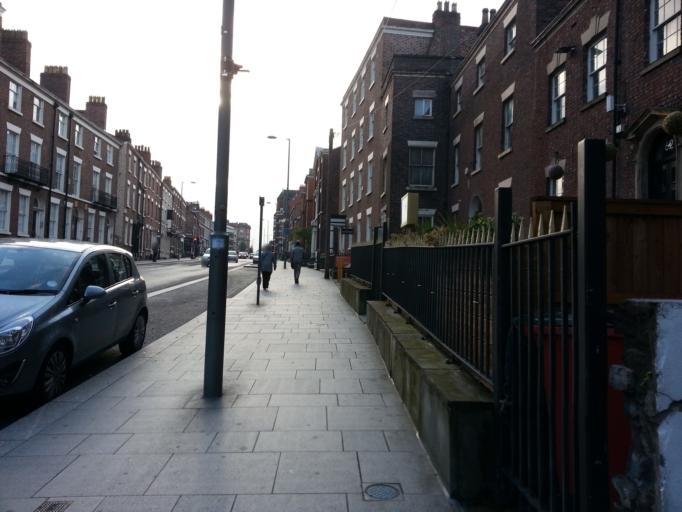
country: GB
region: England
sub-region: Liverpool
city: Liverpool
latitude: 53.4040
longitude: -2.9743
